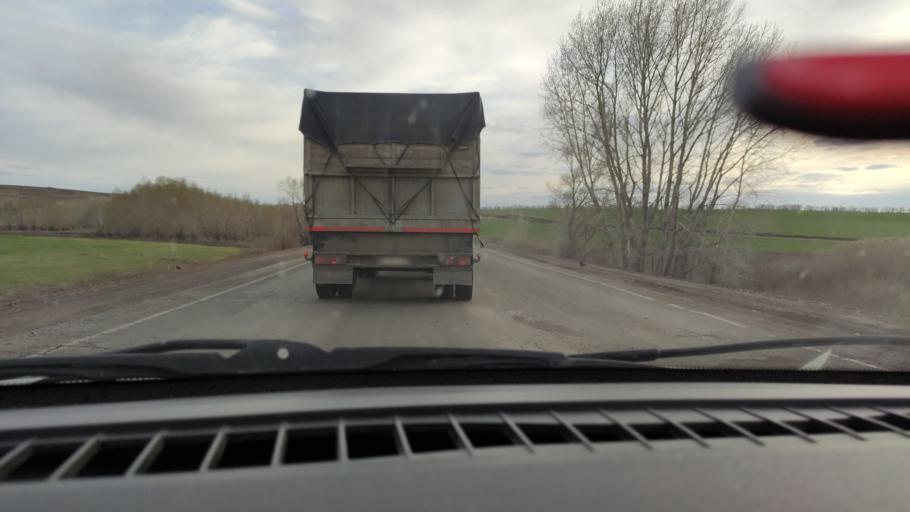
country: RU
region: Orenburg
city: Sakmara
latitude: 52.1897
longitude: 55.2996
